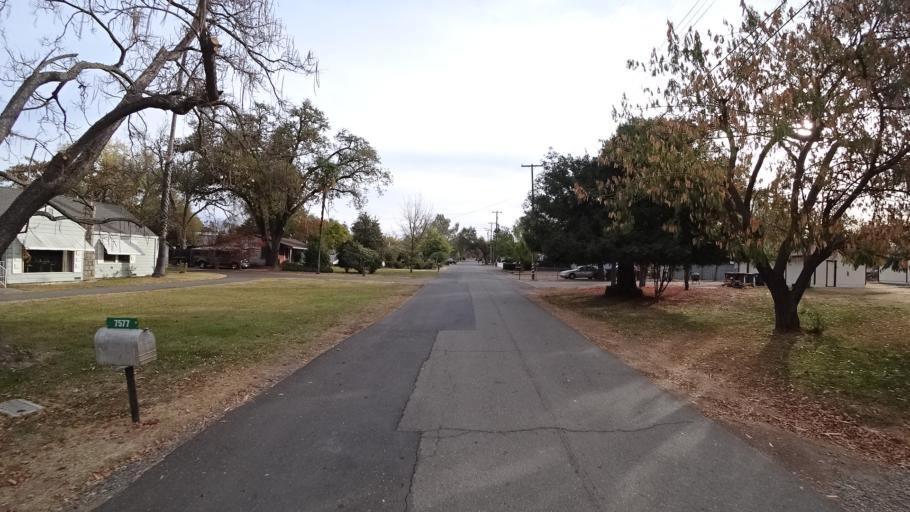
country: US
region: California
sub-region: Sacramento County
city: Citrus Heights
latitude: 38.7203
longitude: -121.2872
